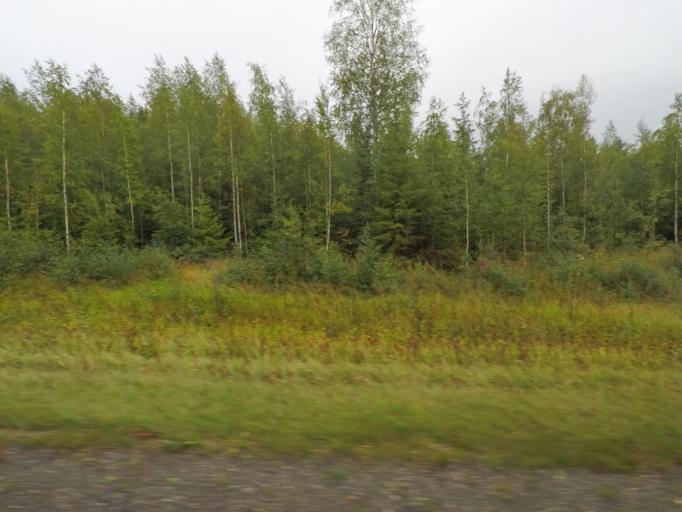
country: FI
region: Southern Savonia
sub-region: Pieksaemaeki
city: Joroinen
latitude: 62.1163
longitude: 27.8375
